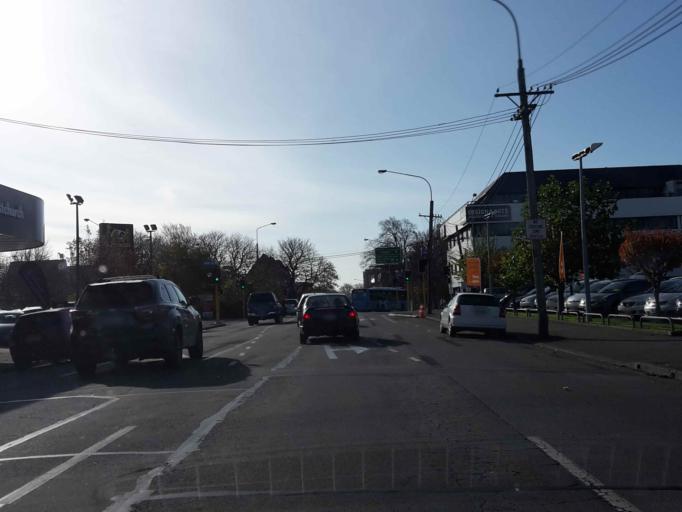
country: NZ
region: Canterbury
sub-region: Christchurch City
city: Christchurch
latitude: -43.5360
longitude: 172.6307
